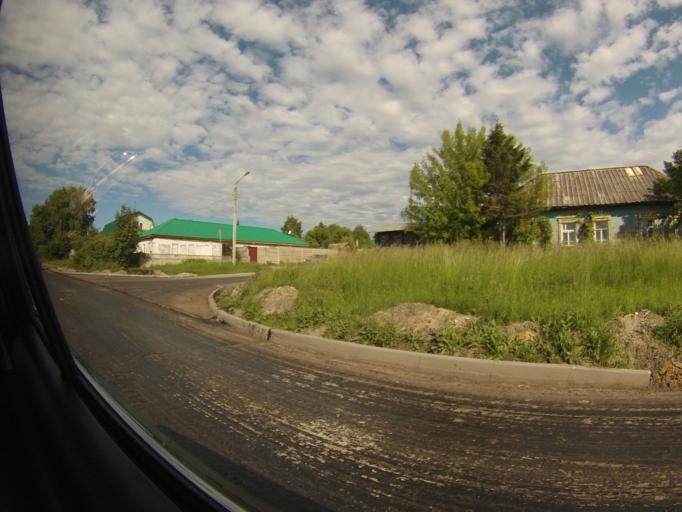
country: RU
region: Orjol
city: Mtsensk
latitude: 53.2872
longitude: 36.5813
